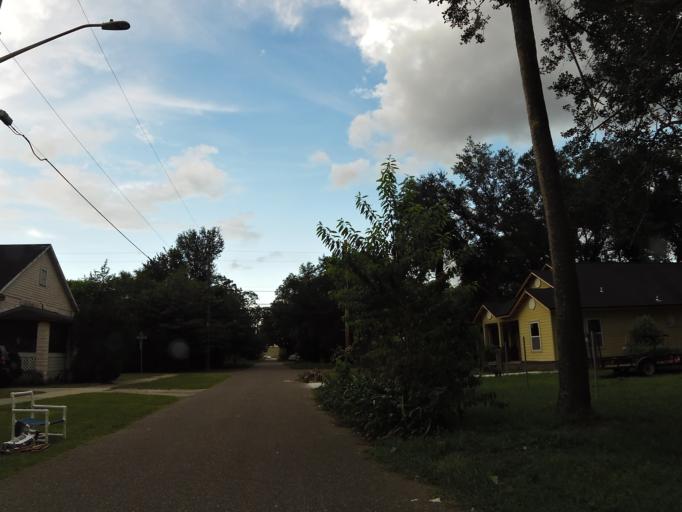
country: US
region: Florida
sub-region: Duval County
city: Jacksonville
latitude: 30.3523
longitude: -81.6352
